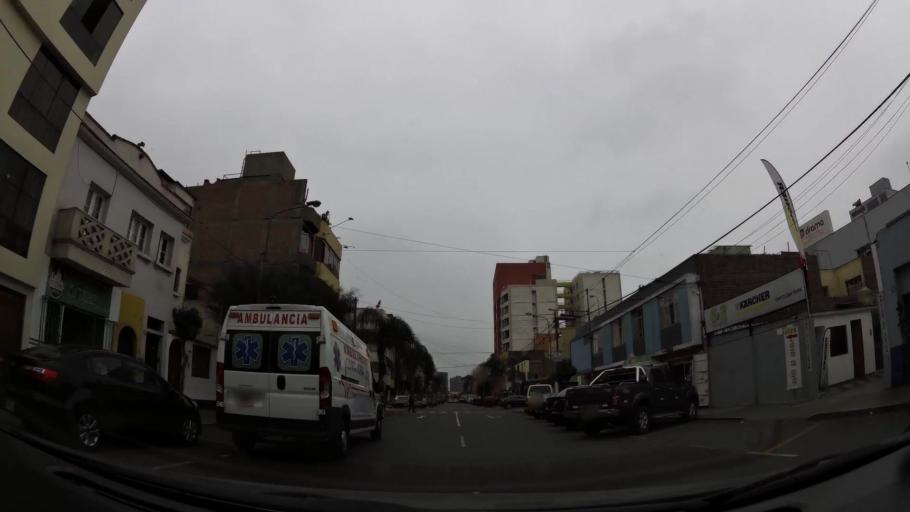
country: PE
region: Lima
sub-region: Lima
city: San Isidro
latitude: -12.0873
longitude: -77.0320
